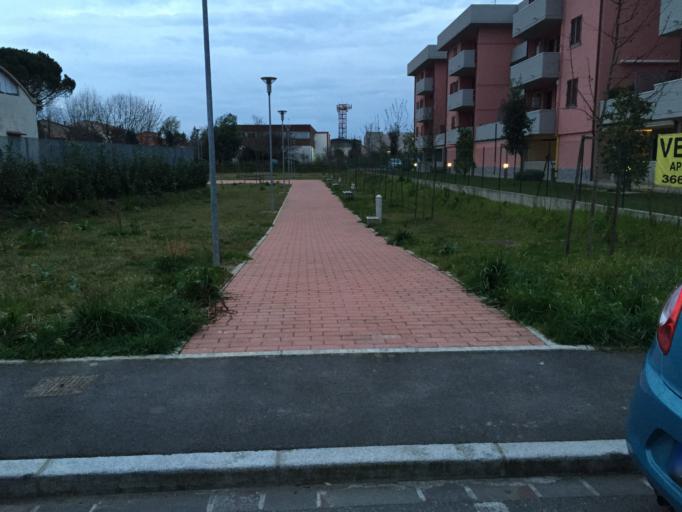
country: IT
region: Tuscany
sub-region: Provincia di Prato
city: Fornacelle
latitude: 43.8860
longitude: 11.0480
